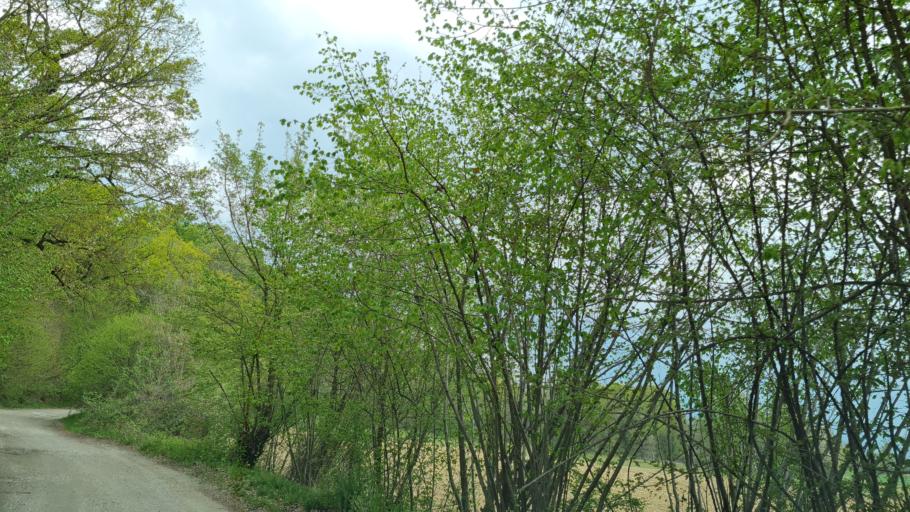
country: IT
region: Piedmont
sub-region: Provincia di Biella
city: Cerrione
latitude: 45.4715
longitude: 8.0651
